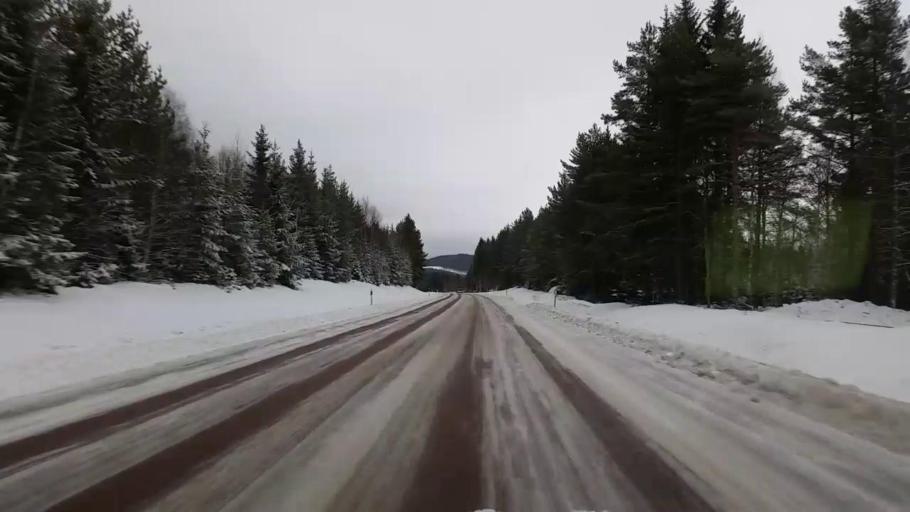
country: SE
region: Gaevleborg
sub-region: Ljusdals Kommun
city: Jaervsoe
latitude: 61.8054
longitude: 16.2557
